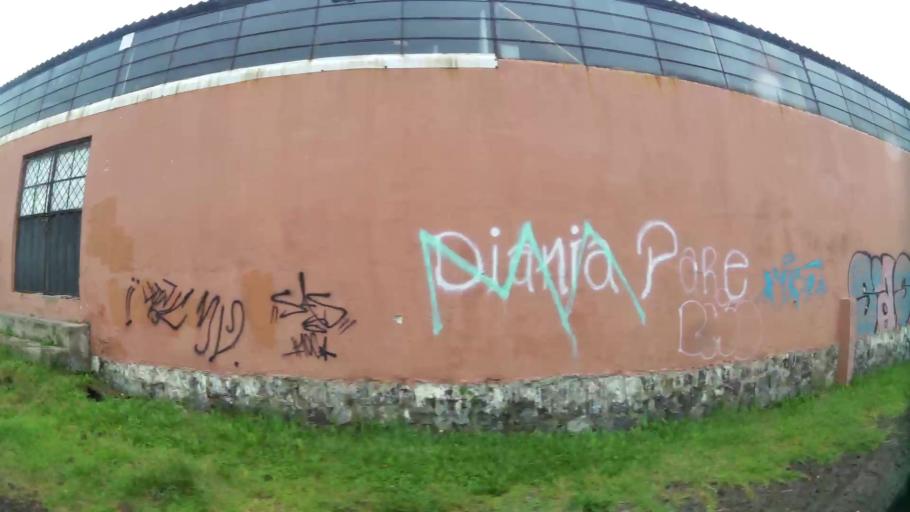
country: EC
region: Pichincha
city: Sangolqui
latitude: -0.2791
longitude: -78.4571
